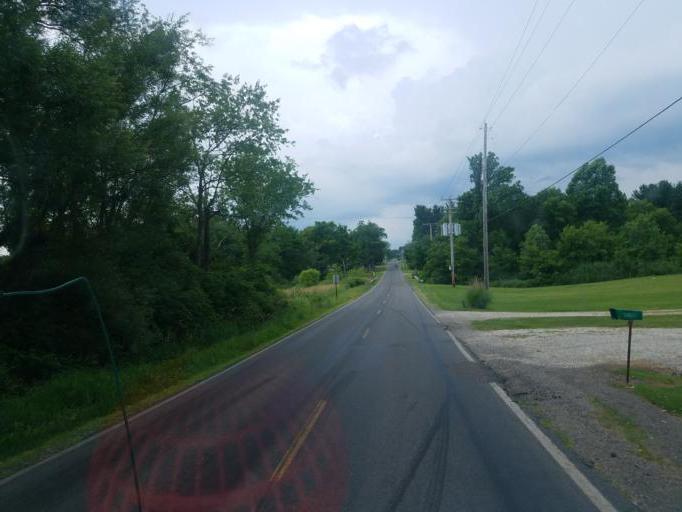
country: US
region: Ohio
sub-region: Stark County
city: Hartville
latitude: 41.0331
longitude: -81.2558
